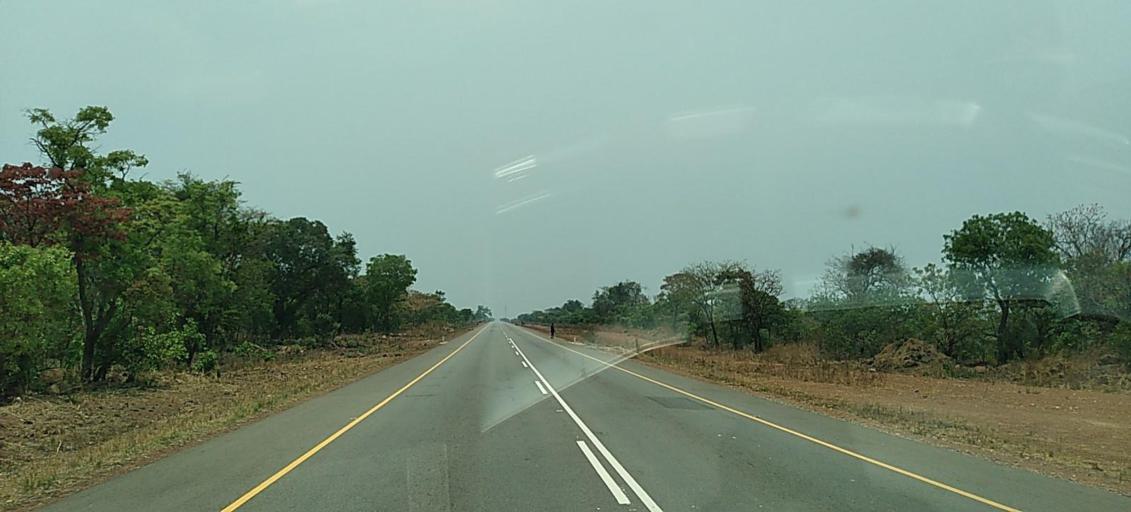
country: ZM
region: Copperbelt
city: Chililabombwe
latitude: -12.3650
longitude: 27.2927
